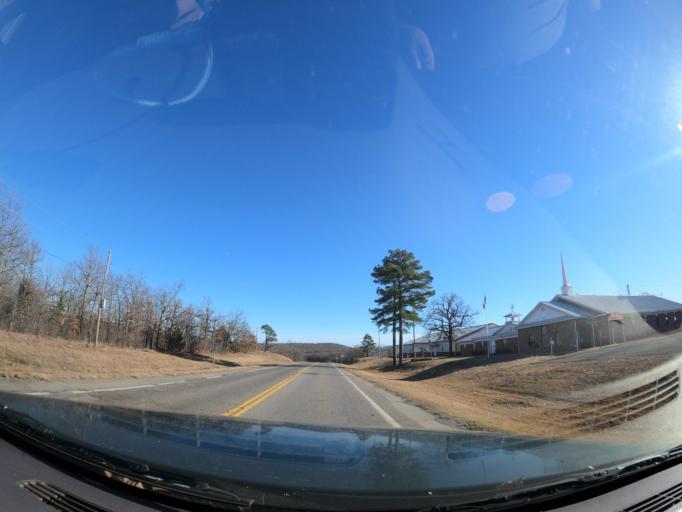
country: US
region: Oklahoma
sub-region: Pittsburg County
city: Longtown
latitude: 35.2287
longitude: -95.4514
